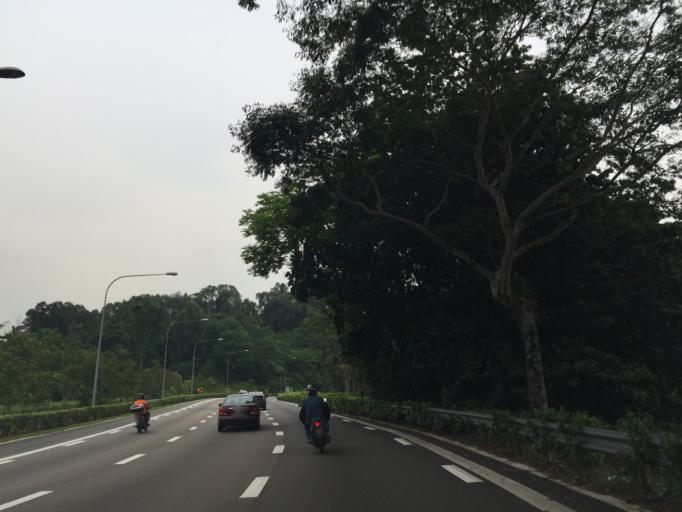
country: SG
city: Singapore
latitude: 1.3489
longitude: 103.7944
